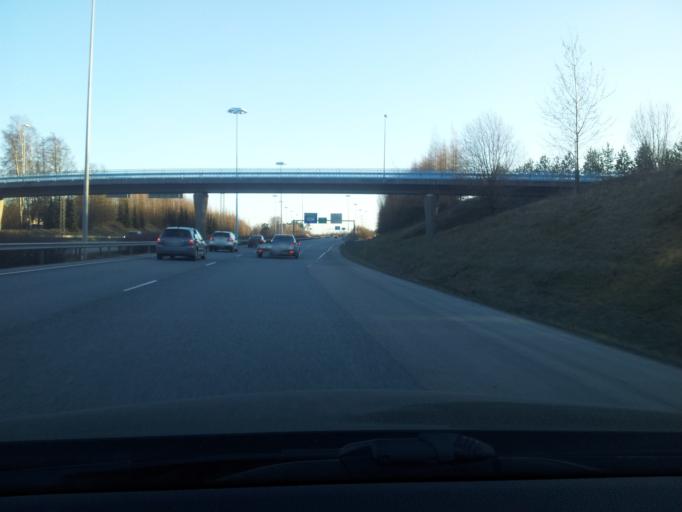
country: FI
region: Uusimaa
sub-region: Helsinki
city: Koukkuniemi
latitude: 60.1747
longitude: 24.7554
